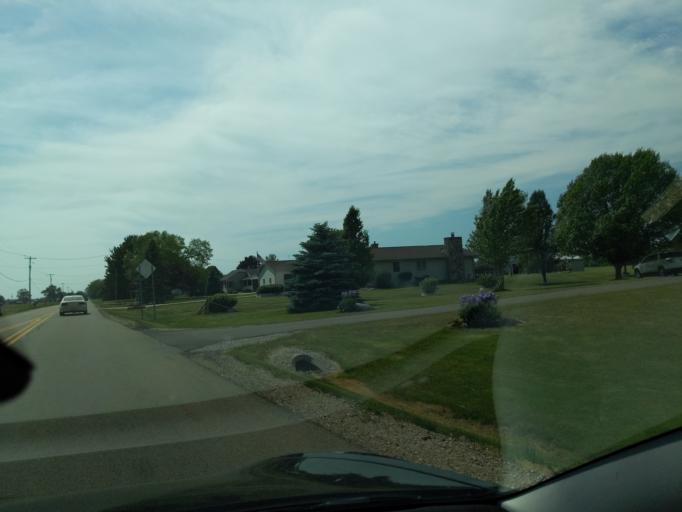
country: US
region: Michigan
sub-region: Eaton County
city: Grand Ledge
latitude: 42.7119
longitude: -84.7416
